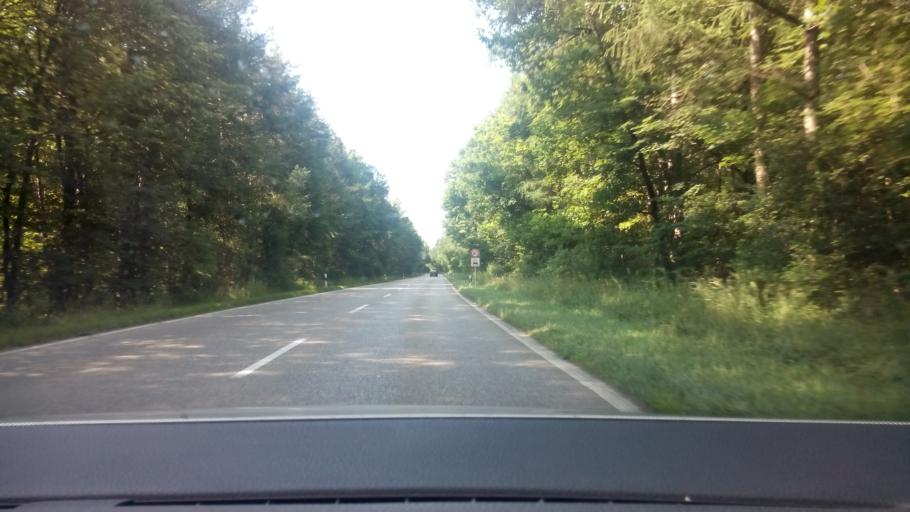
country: DE
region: Bavaria
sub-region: Upper Bavaria
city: Oberschleissheim
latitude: 48.2454
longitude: 11.5830
